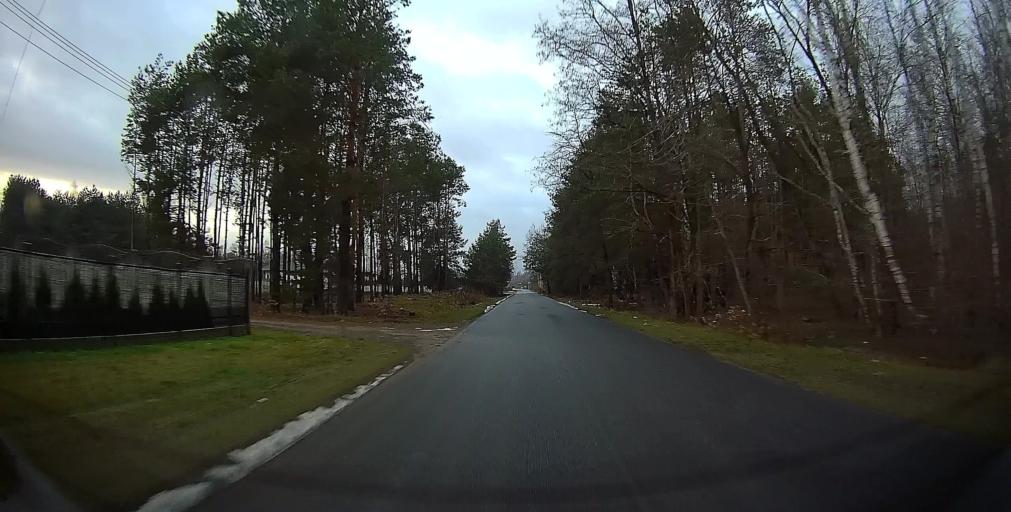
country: PL
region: Masovian Voivodeship
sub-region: Radom
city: Radom
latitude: 51.4528
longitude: 21.1292
